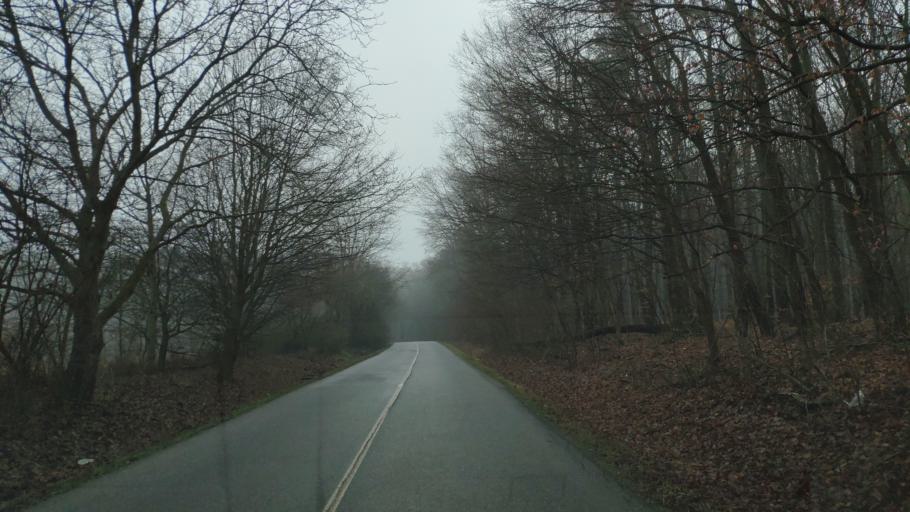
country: SK
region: Kosicky
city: Kosice
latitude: 48.7115
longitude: 21.3720
